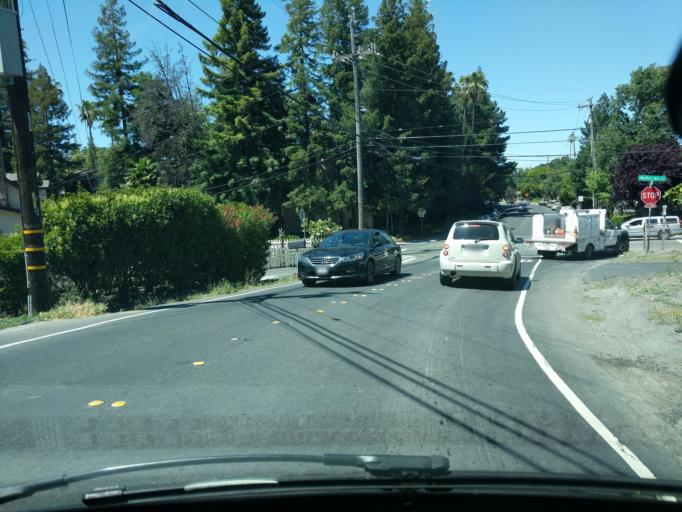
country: US
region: California
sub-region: Contra Costa County
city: Walnut Creek
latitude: 37.8995
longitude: -122.0541
